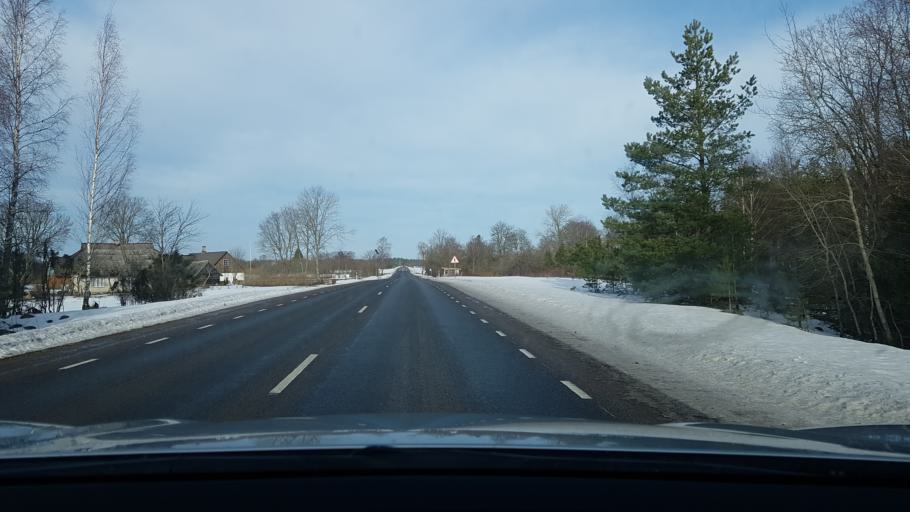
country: EE
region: Saare
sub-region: Kuressaare linn
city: Kuressaare
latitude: 58.3060
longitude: 22.5400
